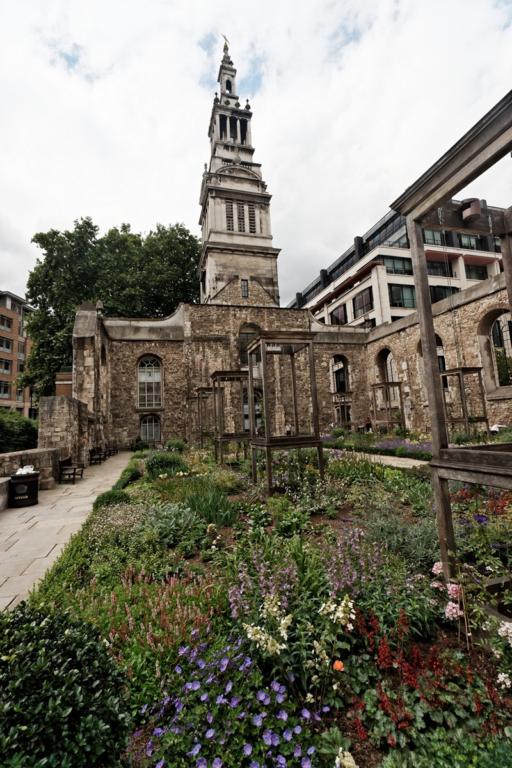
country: GB
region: England
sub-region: Greater London
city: Barbican
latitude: 51.5158
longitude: -0.0988
